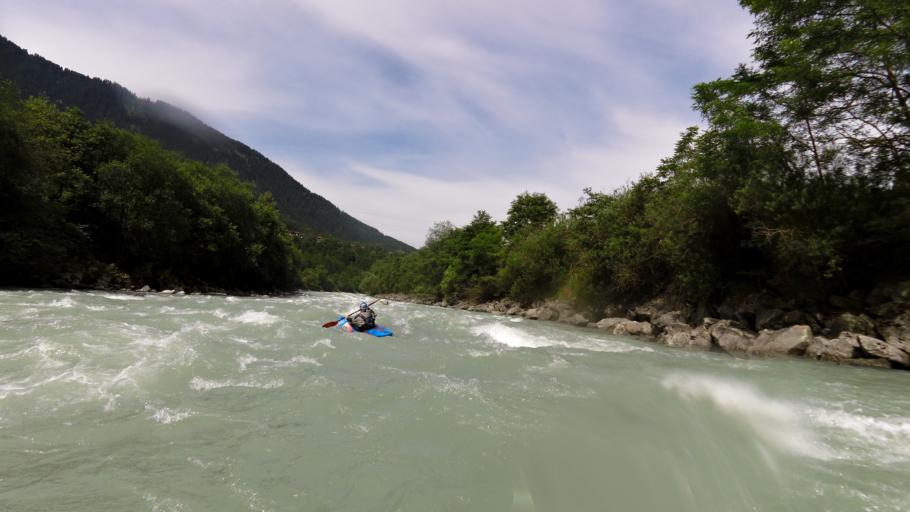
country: AT
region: Tyrol
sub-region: Politischer Bezirk Imst
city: Sautens
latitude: 47.2129
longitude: 10.8686
